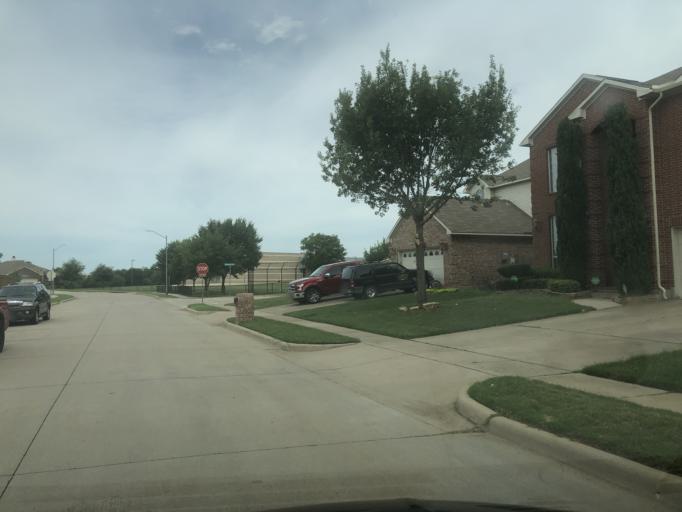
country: US
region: Texas
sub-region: Dallas County
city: Irving
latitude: 32.7976
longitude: -96.9884
